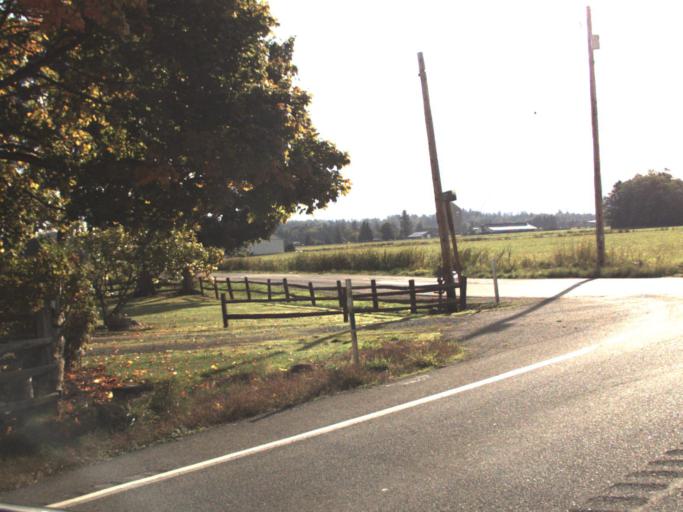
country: US
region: Washington
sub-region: Skagit County
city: Burlington
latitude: 48.5451
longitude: -122.4054
